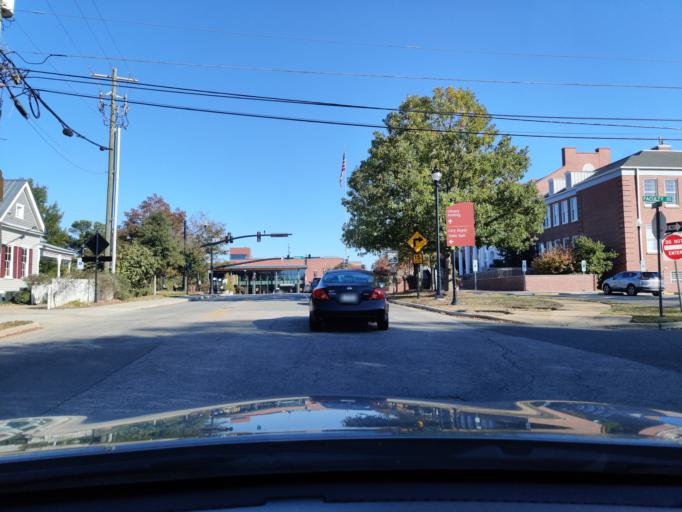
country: US
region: North Carolina
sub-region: Wake County
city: Cary
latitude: 35.7830
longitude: -78.7821
